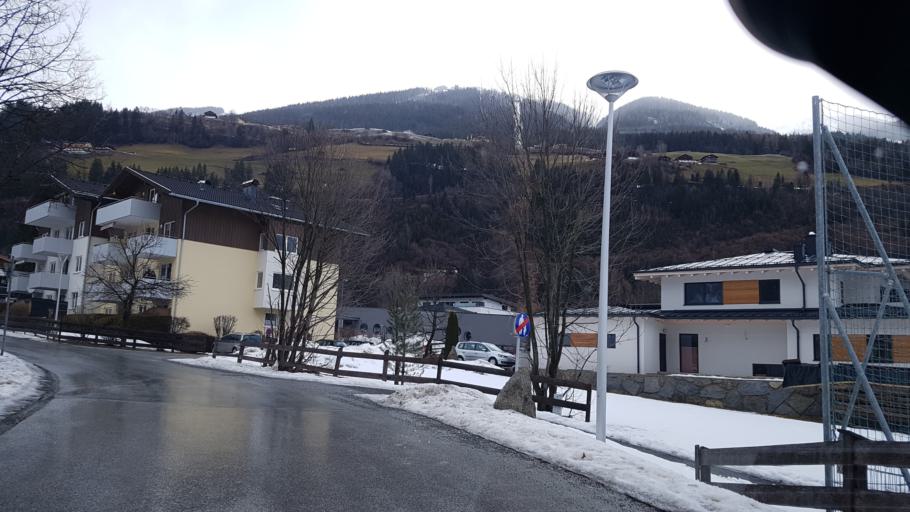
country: AT
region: Salzburg
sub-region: Politischer Bezirk Zell am See
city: Neukirchen am Grossvenediger
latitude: 47.2518
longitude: 12.2806
